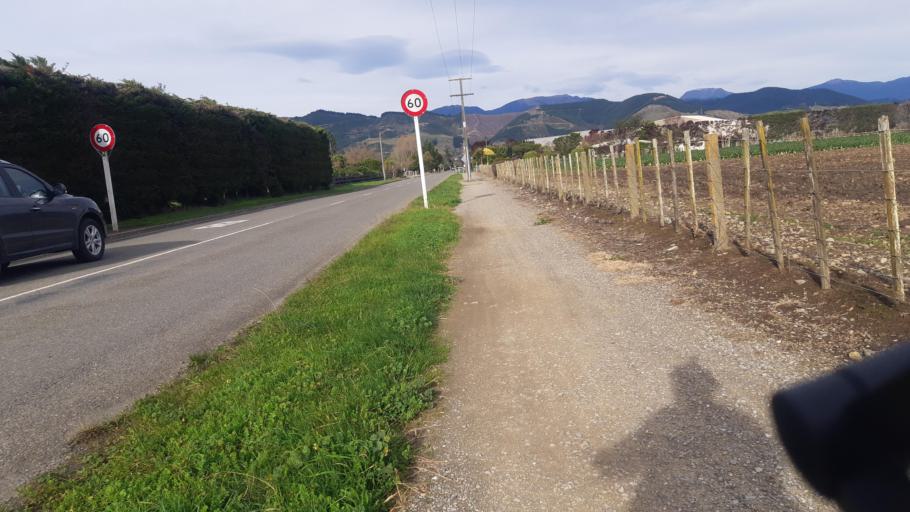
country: NZ
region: Tasman
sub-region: Tasman District
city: Richmond
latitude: -41.3448
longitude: 173.1434
